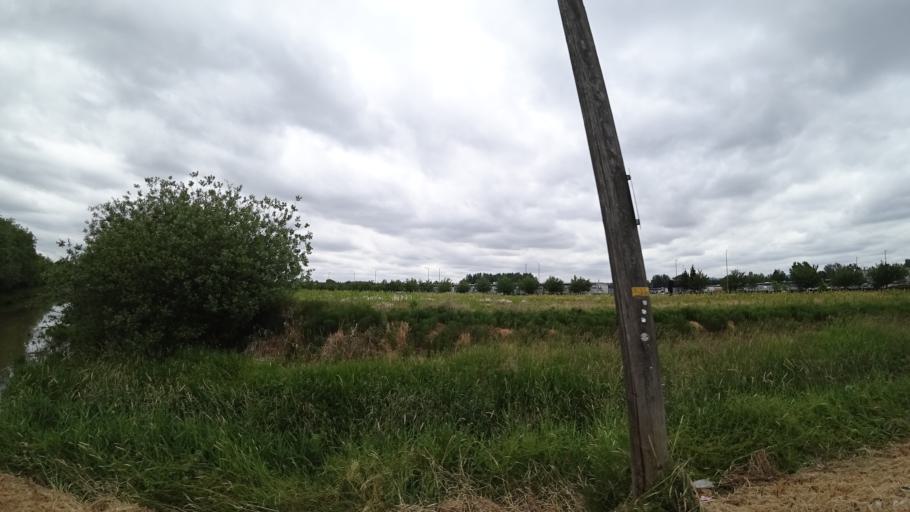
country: US
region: Washington
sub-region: Clark County
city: Vancouver
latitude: 45.5906
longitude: -122.6569
